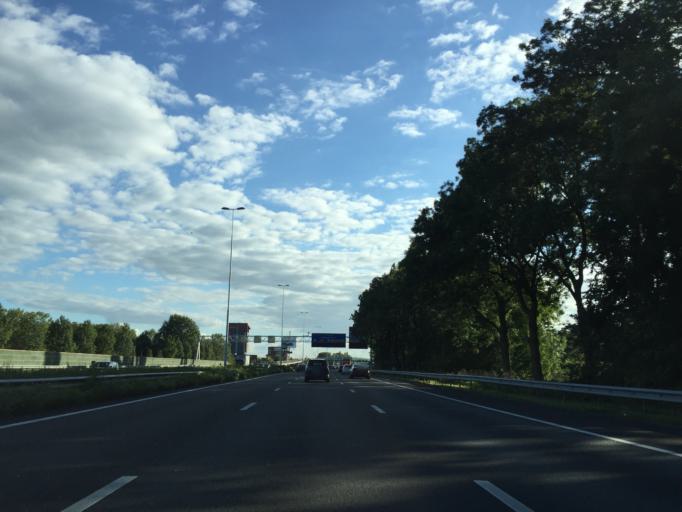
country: NL
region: South Holland
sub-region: Gemeente Dordrecht
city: Dordrecht
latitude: 51.7812
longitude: 4.6506
